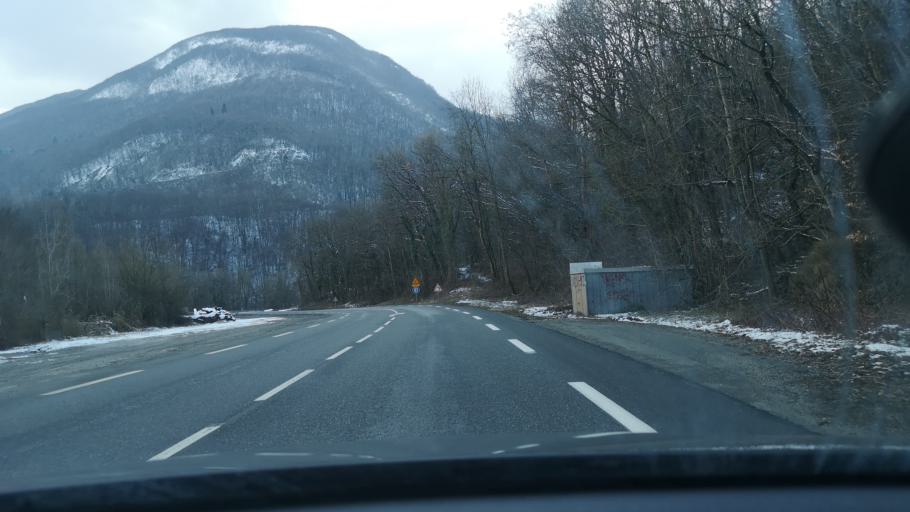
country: FR
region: Rhone-Alpes
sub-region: Departement de l'Ain
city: Collonges
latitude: 46.1227
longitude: 5.9040
